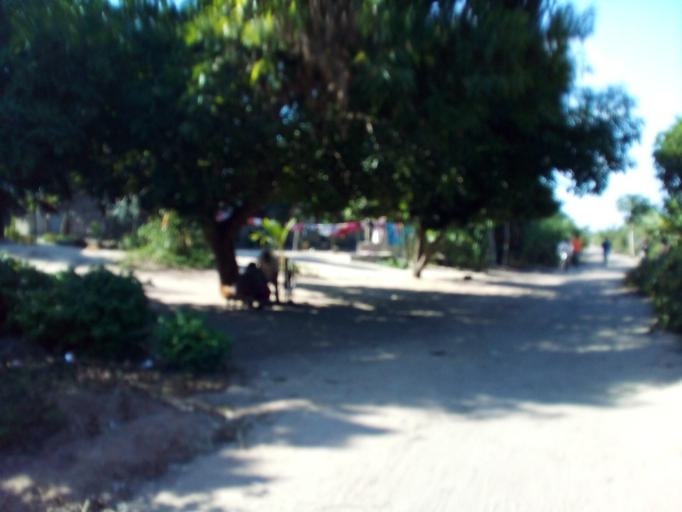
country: MZ
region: Zambezia
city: Quelimane
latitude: -17.5967
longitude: 36.8289
